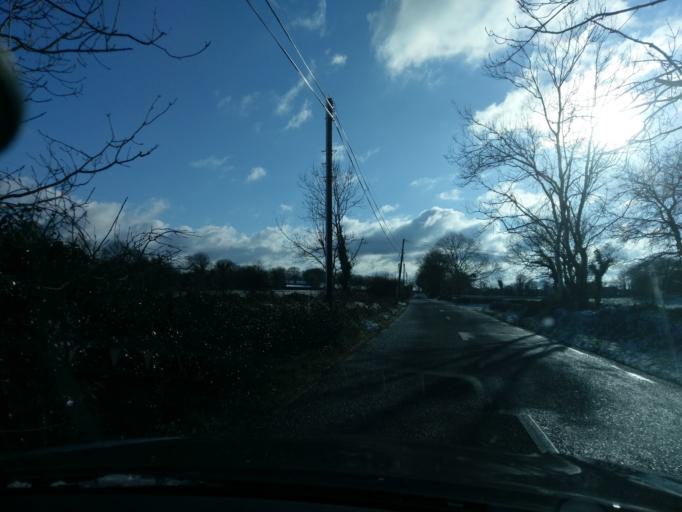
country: IE
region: Connaught
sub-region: County Galway
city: Gort
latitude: 53.1766
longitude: -8.7870
